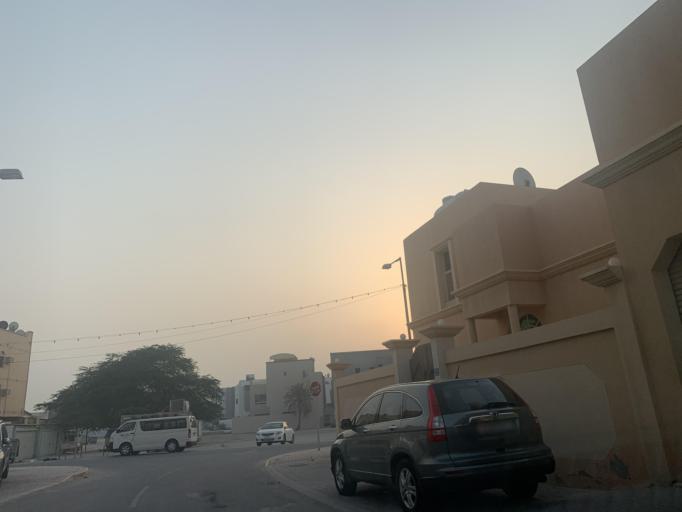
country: BH
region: Manama
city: Jidd Hafs
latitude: 26.2247
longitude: 50.5133
